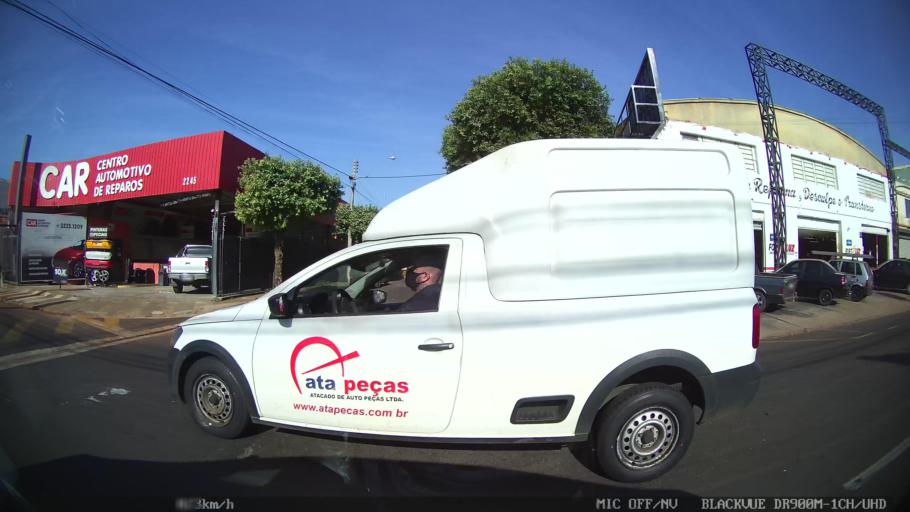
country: BR
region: Sao Paulo
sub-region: Sao Jose Do Rio Preto
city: Sao Jose do Rio Preto
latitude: -20.7995
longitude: -49.3682
